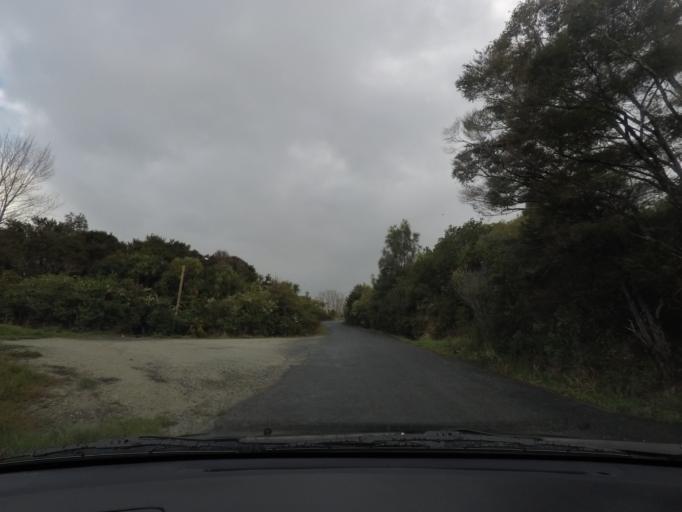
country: NZ
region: Auckland
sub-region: Auckland
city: Warkworth
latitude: -36.4325
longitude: 174.7312
